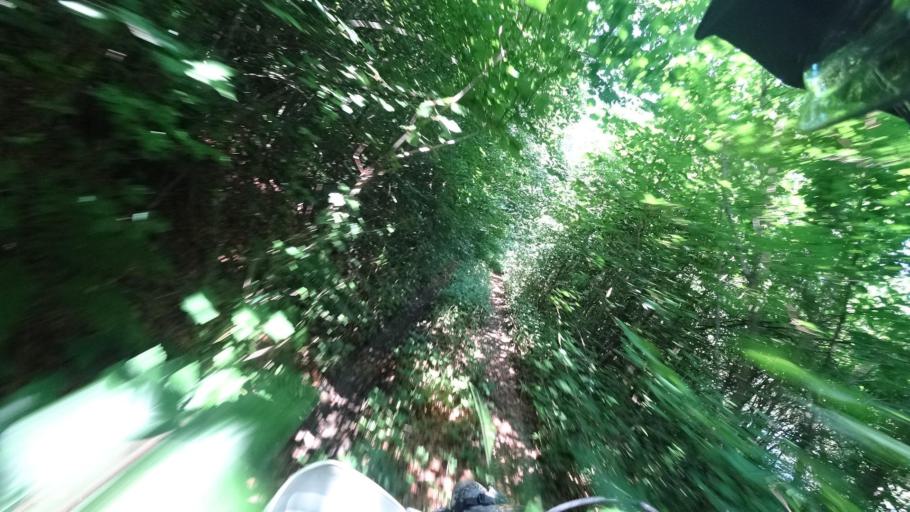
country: HR
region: Karlovacka
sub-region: Grad Ogulin
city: Ogulin
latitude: 45.3074
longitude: 15.1770
